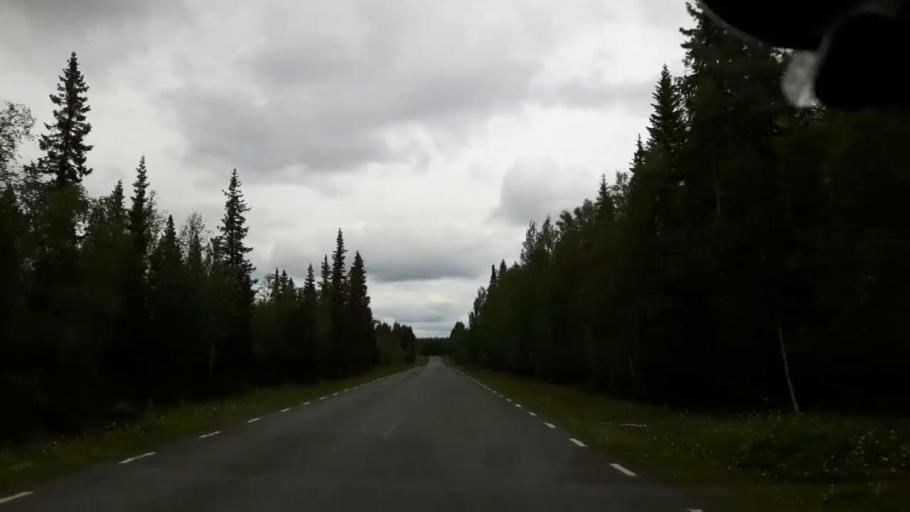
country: SE
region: Jaemtland
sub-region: Krokoms Kommun
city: Valla
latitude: 63.5515
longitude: 13.8501
